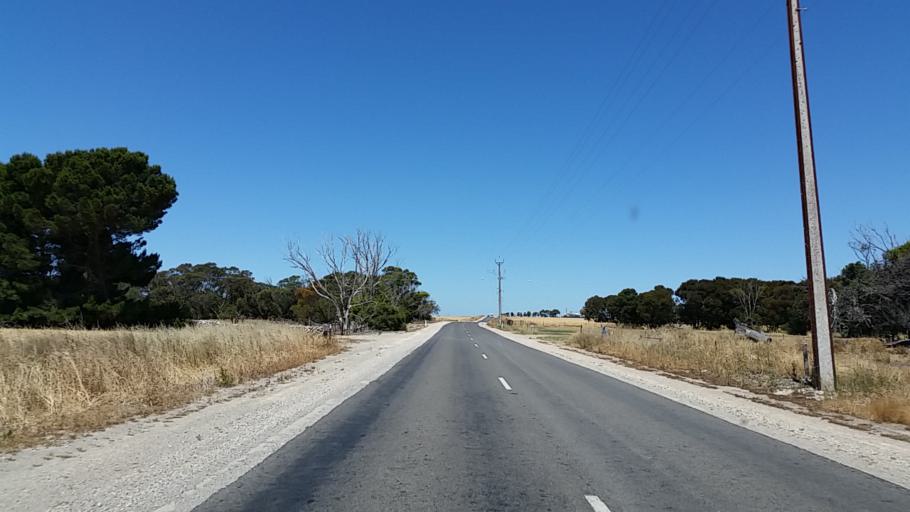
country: AU
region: South Australia
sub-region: Yorke Peninsula
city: Honiton
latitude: -35.0135
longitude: 137.6315
